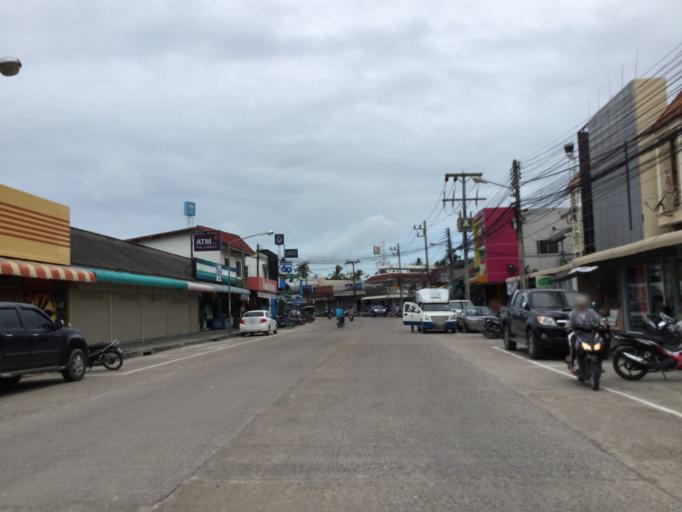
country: TH
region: Surat Thani
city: Ko Pha-Ngan
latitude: 9.7116
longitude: 99.9877
